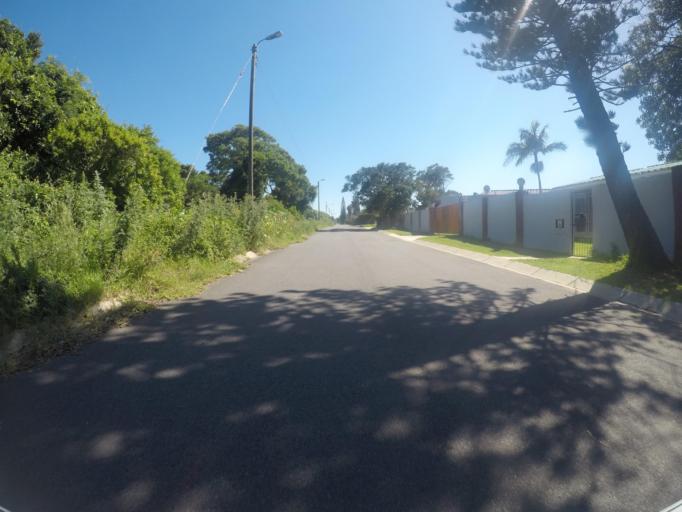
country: ZA
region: Eastern Cape
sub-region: Buffalo City Metropolitan Municipality
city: East London
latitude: -32.9476
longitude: 28.0016
